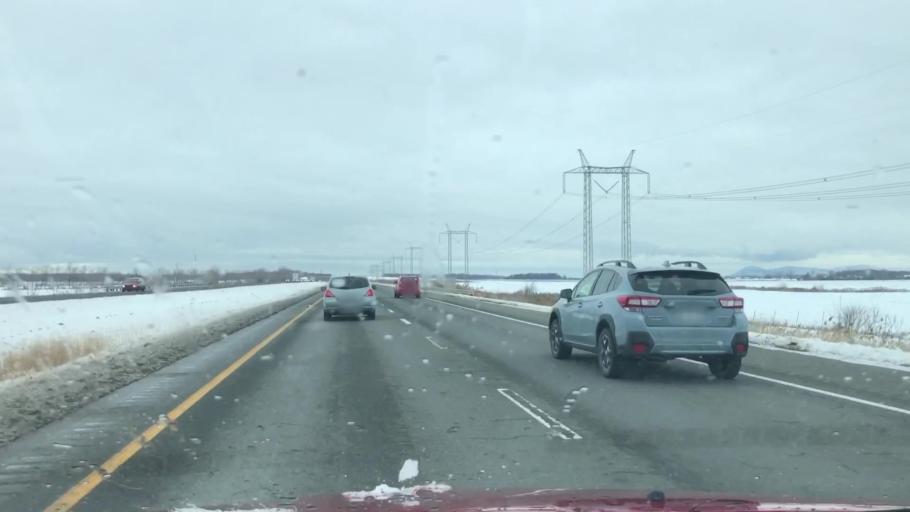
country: CA
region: Quebec
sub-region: Monteregie
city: Rougemont
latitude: 45.3755
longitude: -73.0459
